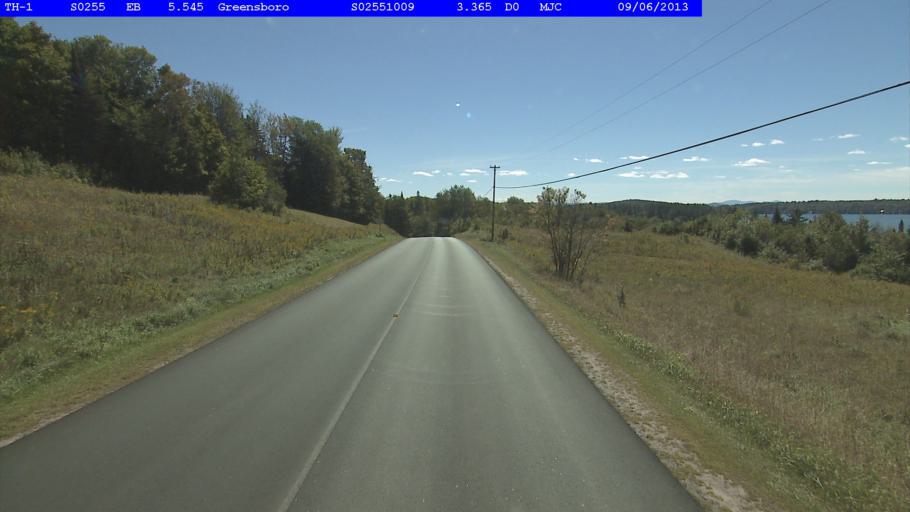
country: US
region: Vermont
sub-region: Caledonia County
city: Hardwick
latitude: 44.5993
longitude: -72.3052
